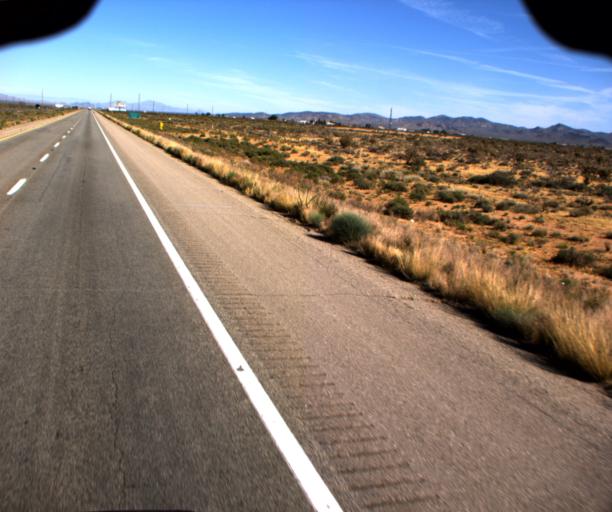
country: US
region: Arizona
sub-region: Mohave County
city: Dolan Springs
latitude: 35.5262
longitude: -114.3498
